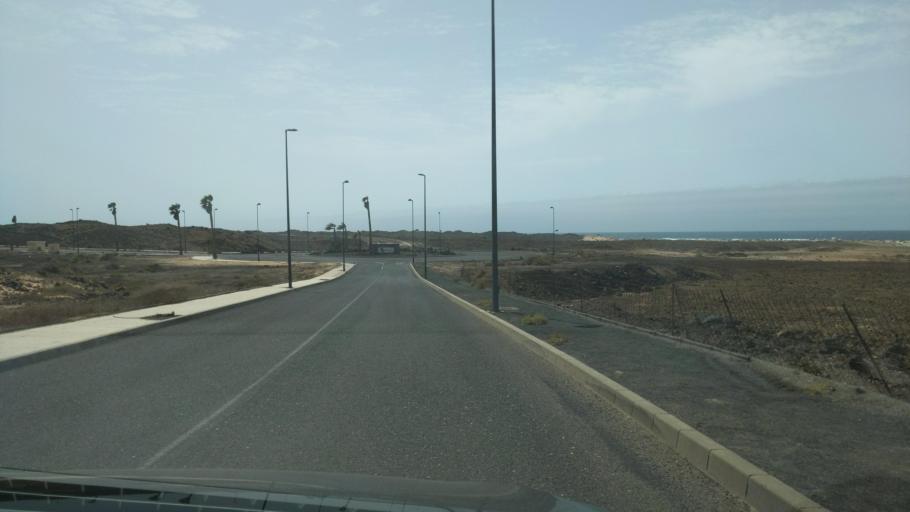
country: ES
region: Canary Islands
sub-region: Provincia de Las Palmas
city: Corralejo
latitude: 28.7375
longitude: -13.9434
